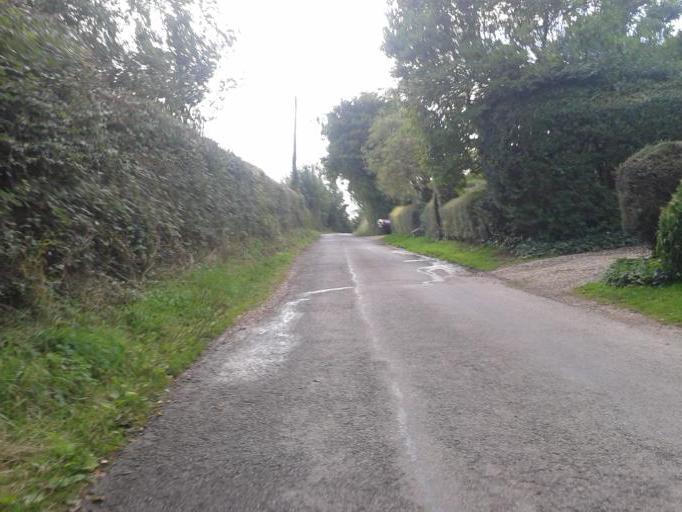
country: GB
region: England
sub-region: Hertfordshire
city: Reed
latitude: 51.9878
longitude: 0.0899
